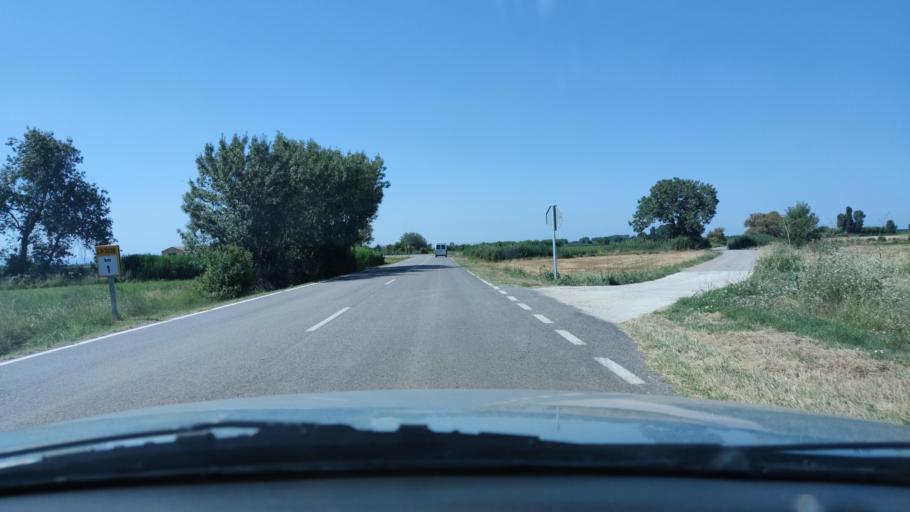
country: ES
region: Catalonia
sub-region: Provincia de Lleida
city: Castellsera
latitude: 41.7385
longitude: 0.9851
